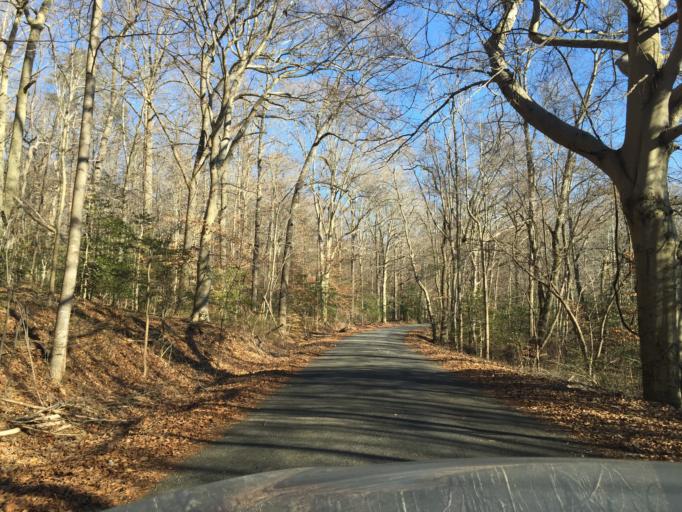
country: US
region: Maryland
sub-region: Anne Arundel County
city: Fort Meade
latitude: 39.0472
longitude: -76.7554
